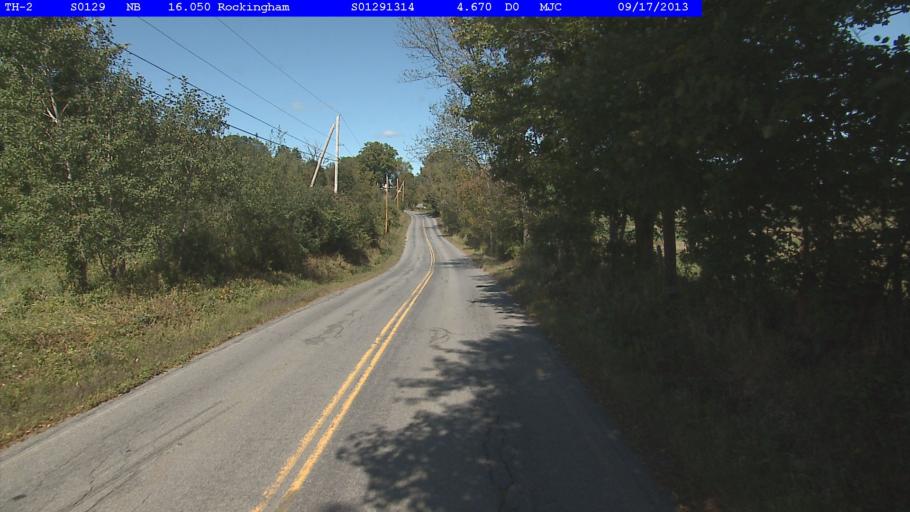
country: US
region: Vermont
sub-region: Windham County
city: Rockingham
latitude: 43.1838
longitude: -72.5131
